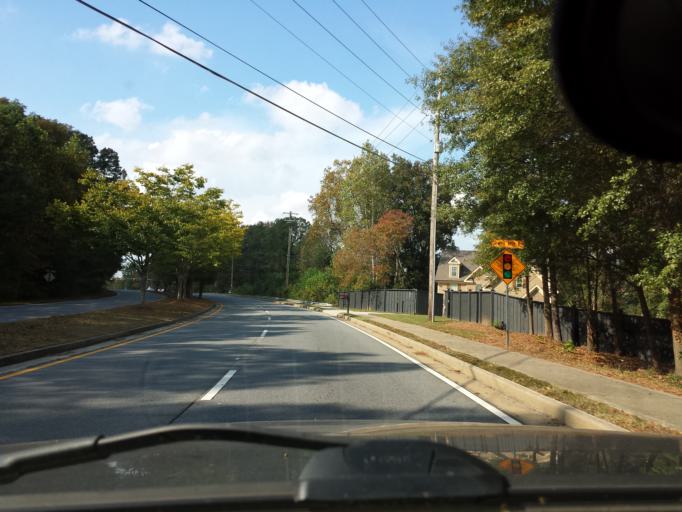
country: US
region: Georgia
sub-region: Cobb County
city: Marietta
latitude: 33.9788
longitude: -84.4800
